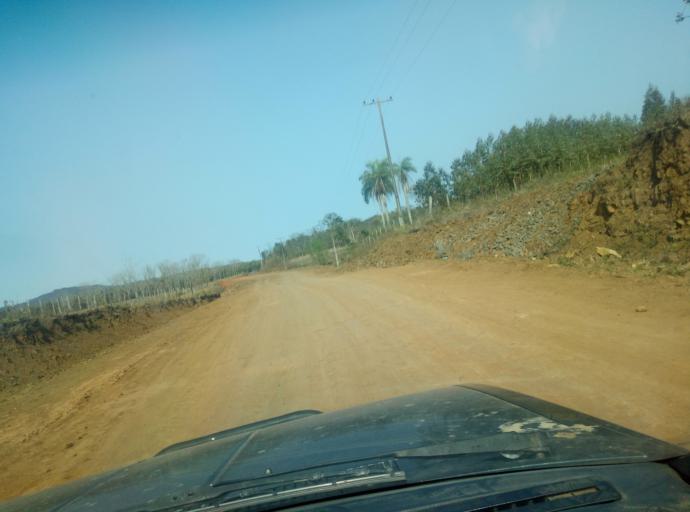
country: PY
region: Caaguazu
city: Coronel Oviedo
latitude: -25.3332
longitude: -56.3144
